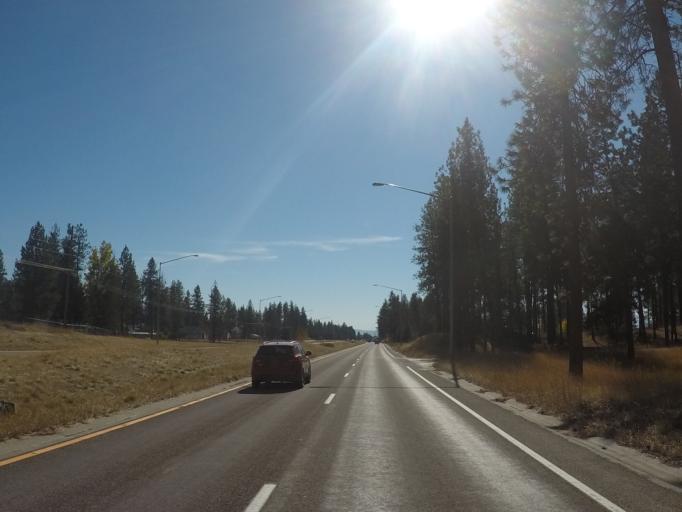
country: US
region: Montana
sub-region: Lake County
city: Pablo
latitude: 47.6097
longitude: -114.1133
